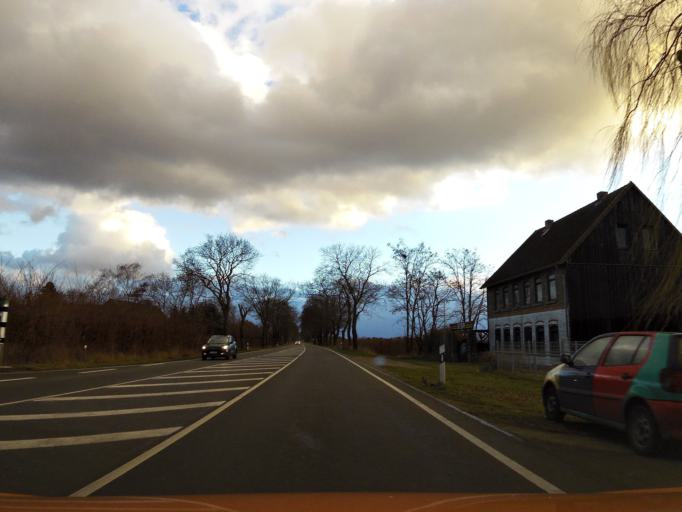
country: DE
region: Lower Saxony
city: Didderse
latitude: 52.3783
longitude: 10.3805
